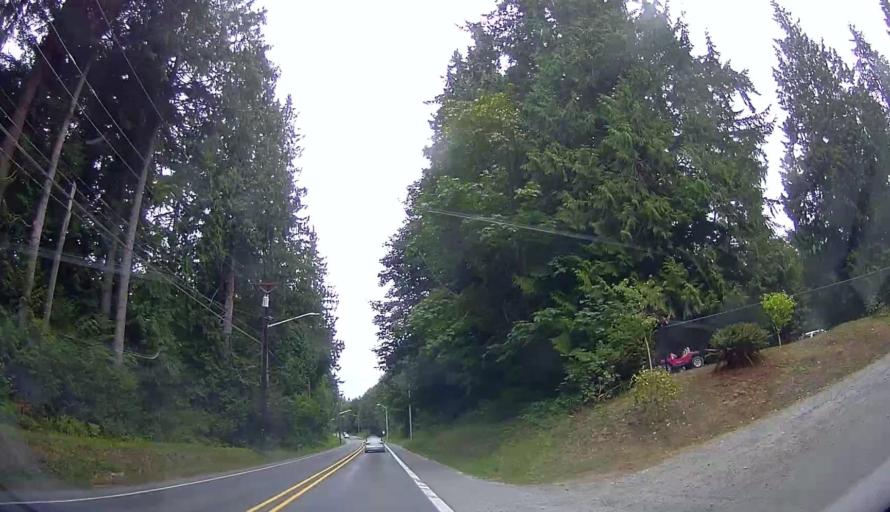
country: US
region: Washington
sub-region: Snohomish County
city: Tulalip
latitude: 48.0466
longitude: -122.2545
